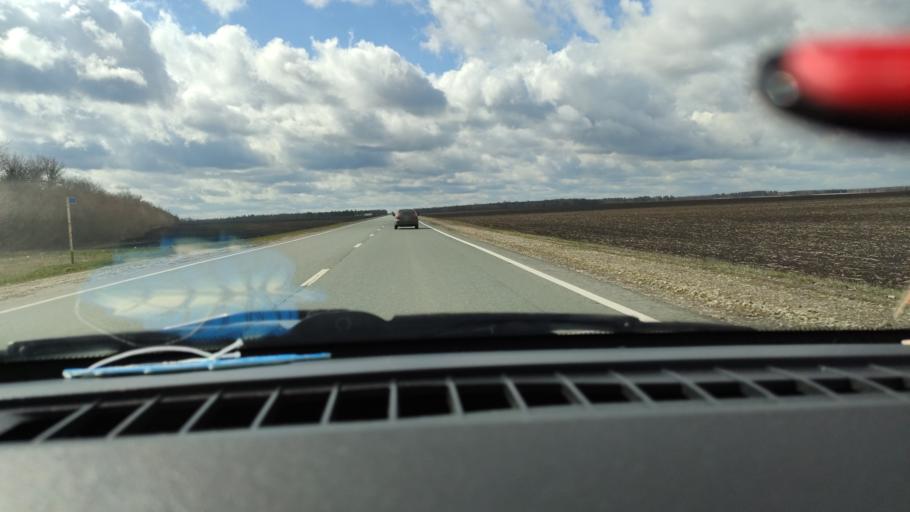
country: RU
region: Samara
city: Yelkhovka
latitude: 53.7653
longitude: 50.2308
